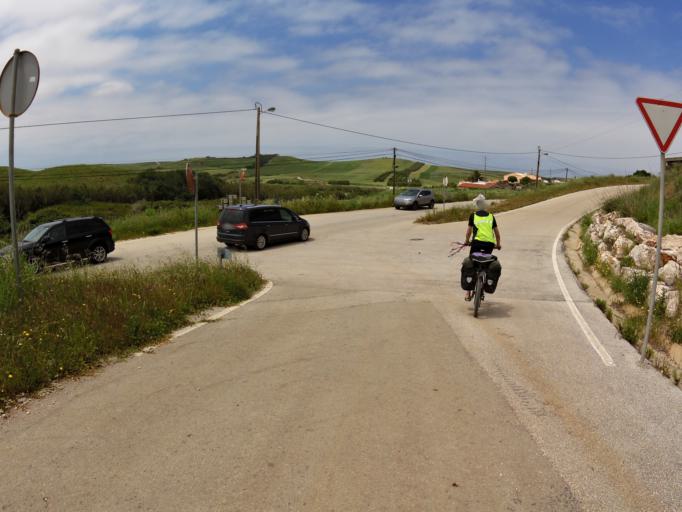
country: PT
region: Faro
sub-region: Vila do Bispo
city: Vila do Bispo
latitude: 37.0795
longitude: -8.8873
